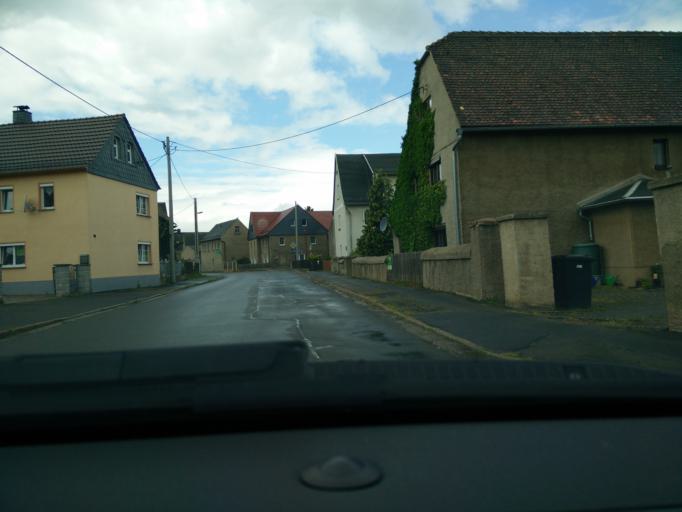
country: DE
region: Saxony
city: Grossbothen
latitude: 51.1878
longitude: 12.7458
